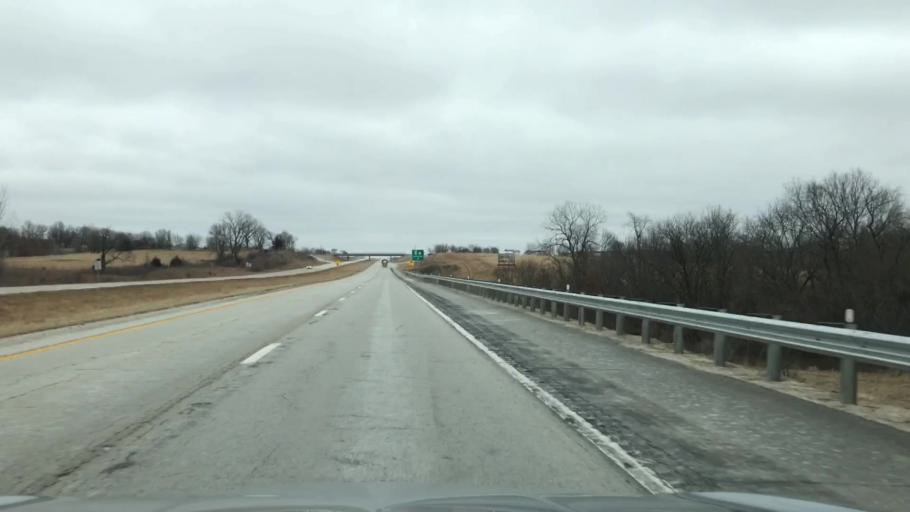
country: US
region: Missouri
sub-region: Caldwell County
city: Hamilton
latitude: 39.7340
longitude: -94.0095
